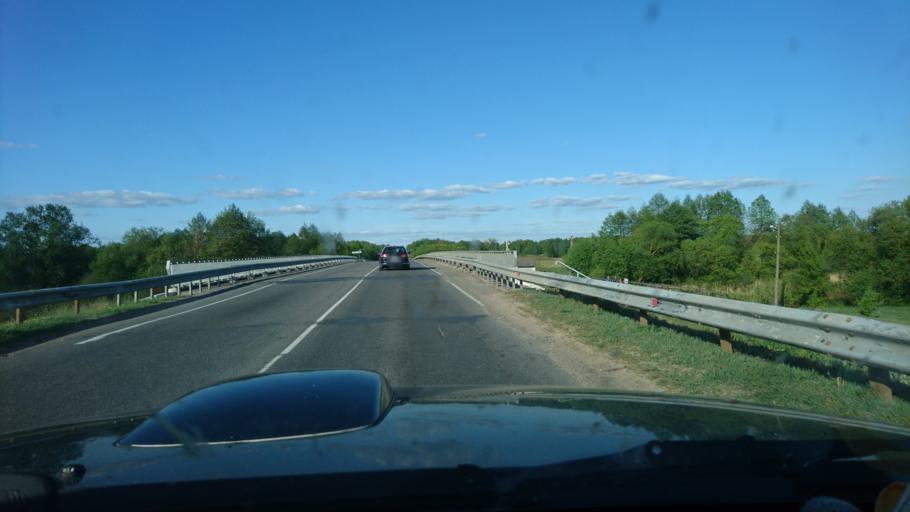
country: BY
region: Brest
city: Byaroza
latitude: 52.5413
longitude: 24.9987
